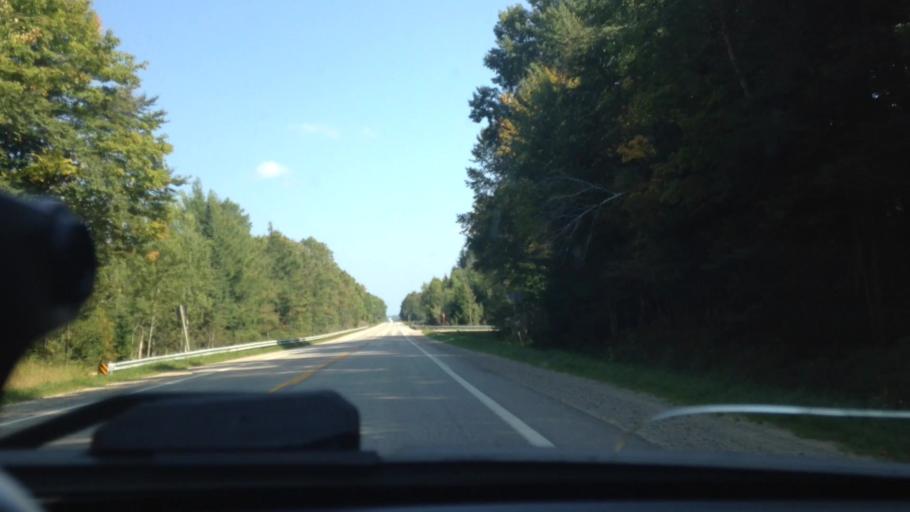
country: US
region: Michigan
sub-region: Luce County
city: Newberry
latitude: 46.3102
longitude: -85.6485
